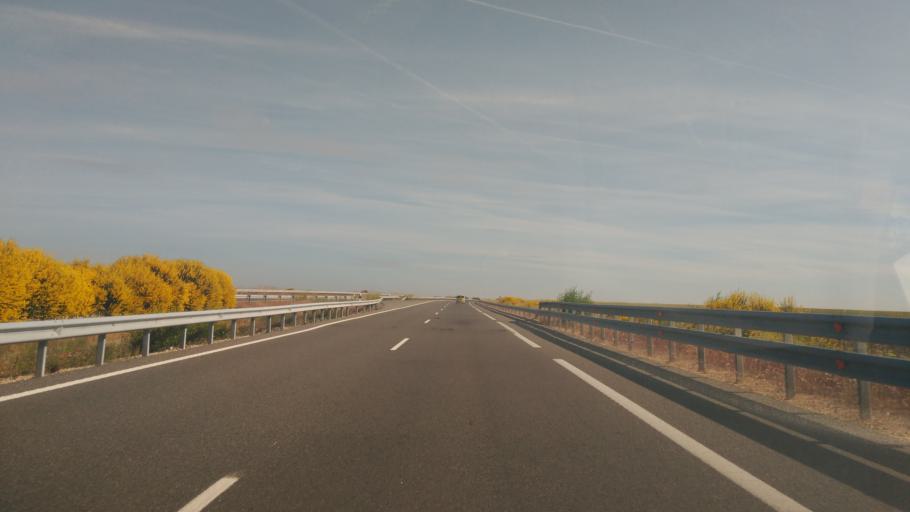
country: ES
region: Castille and Leon
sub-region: Provincia de Salamanca
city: Villamayor
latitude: 41.0141
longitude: -5.6792
